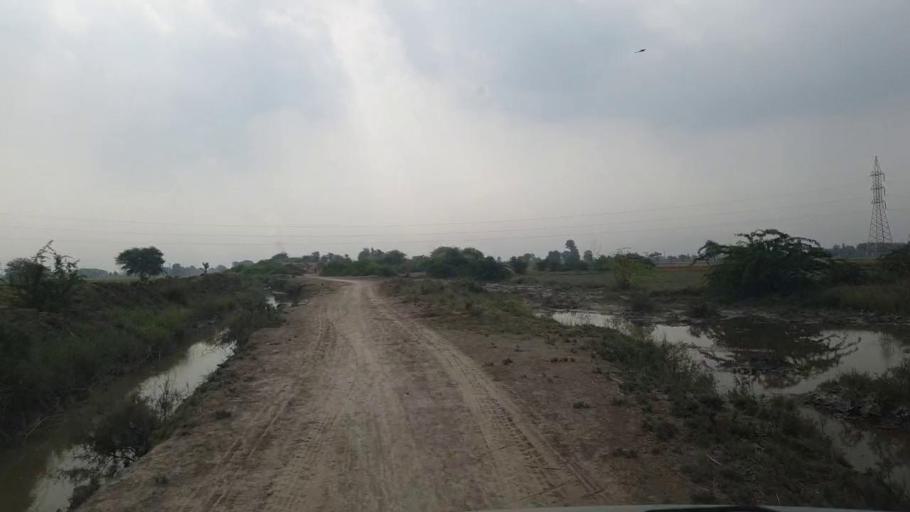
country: PK
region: Sindh
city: Talhar
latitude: 24.8823
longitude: 68.7881
